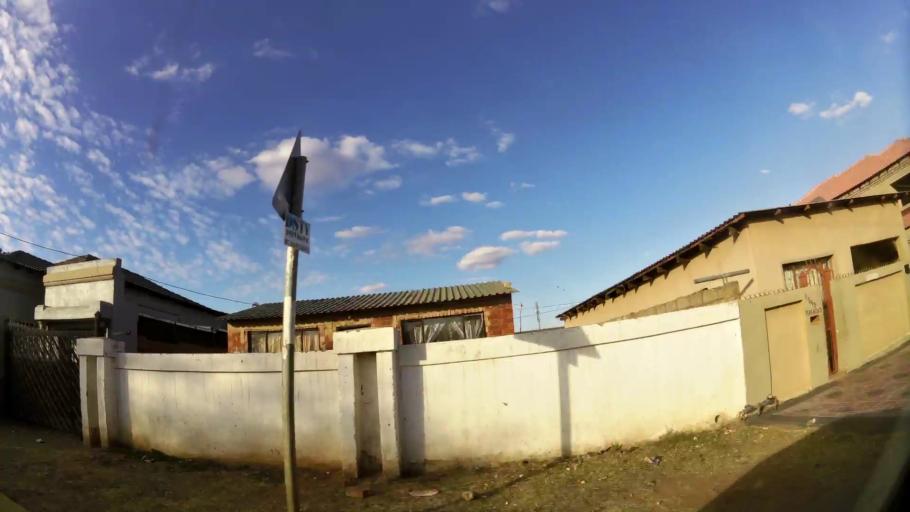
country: ZA
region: Gauteng
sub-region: City of Tshwane Metropolitan Municipality
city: Cullinan
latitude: -25.7059
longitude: 28.3794
